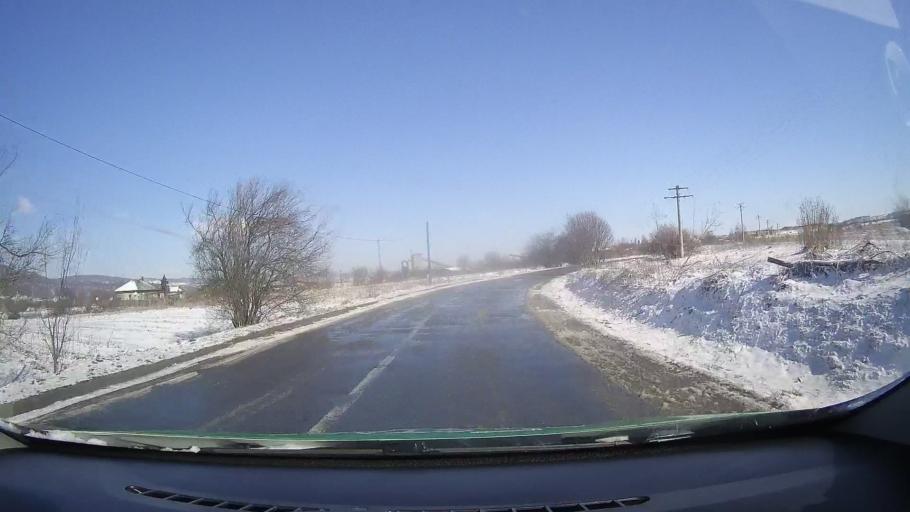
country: RO
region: Sibiu
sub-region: Comuna Racovita
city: Racovita
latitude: 45.6693
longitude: 24.3182
